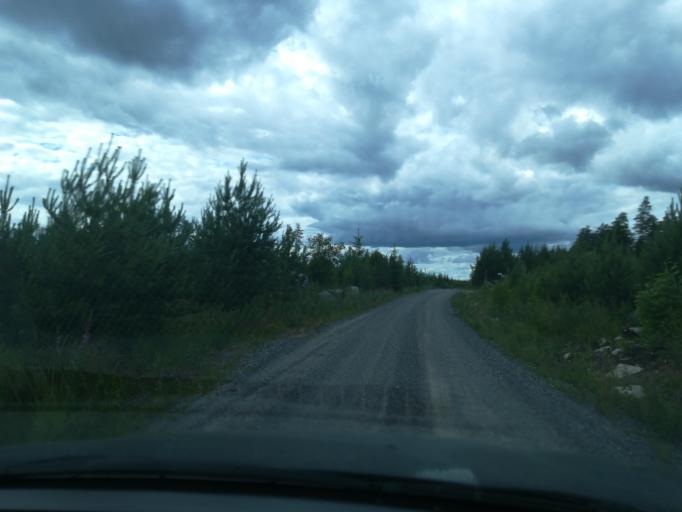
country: FI
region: Southern Savonia
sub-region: Mikkeli
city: Mikkeli
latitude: 61.6690
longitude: 27.1201
